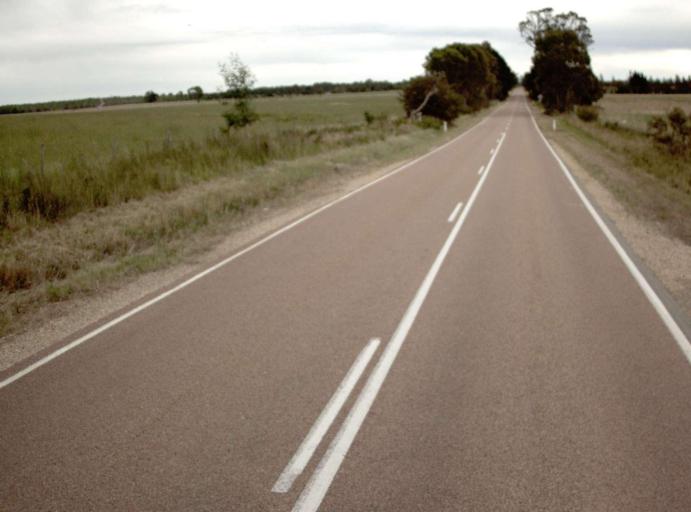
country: AU
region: Victoria
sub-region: East Gippsland
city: Bairnsdale
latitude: -37.9974
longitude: 147.3579
